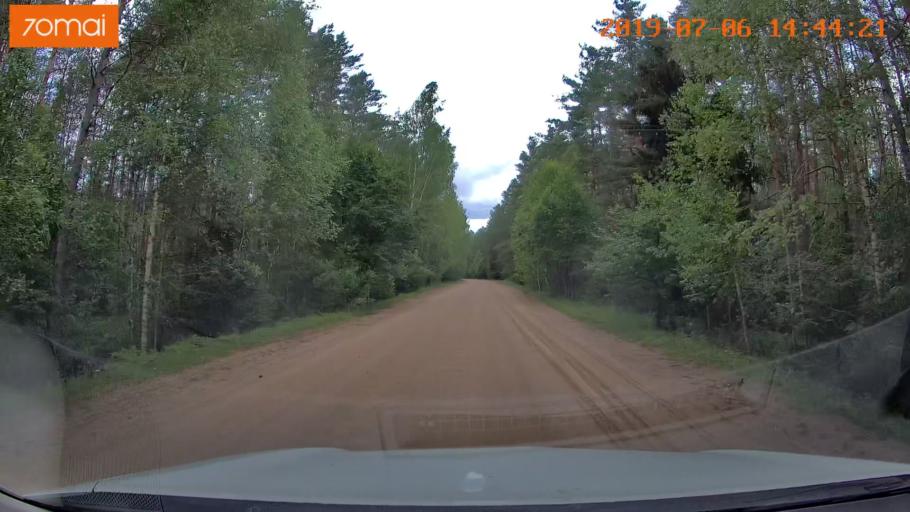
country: BY
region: Minsk
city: Ivyanyets
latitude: 53.9609
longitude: 26.6944
